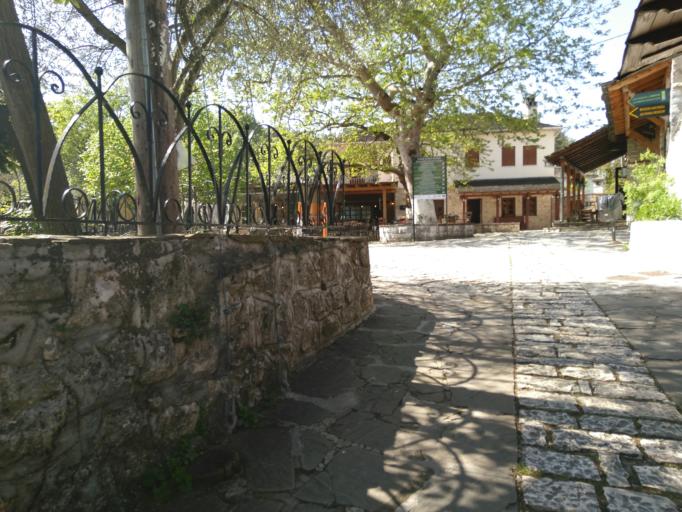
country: GR
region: Epirus
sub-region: Nomos Ioanninon
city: Ioannina
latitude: 39.6811
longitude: 20.8745
